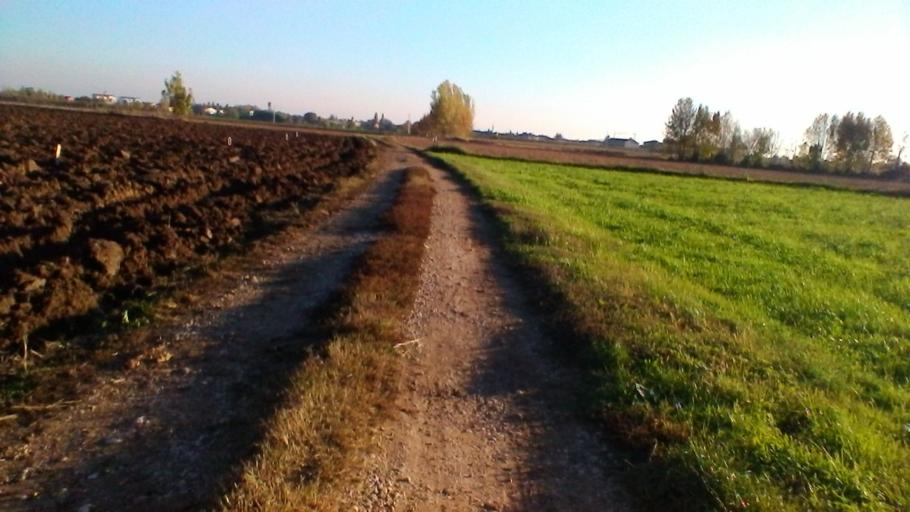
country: IT
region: Veneto
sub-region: Provincia di Verona
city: Povegliano Veronese
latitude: 45.3585
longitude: 10.8752
